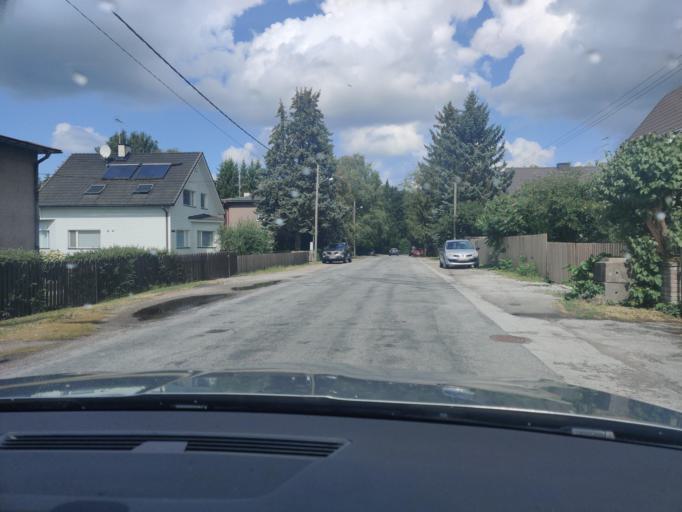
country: EE
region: Harju
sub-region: Saue vald
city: Laagri
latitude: 59.3515
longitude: 24.6231
